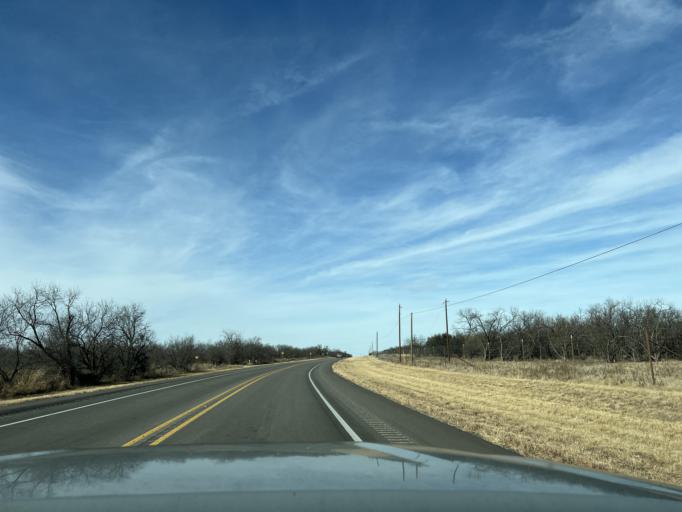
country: US
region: Texas
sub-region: Shackelford County
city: Albany
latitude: 32.6293
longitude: -99.2252
